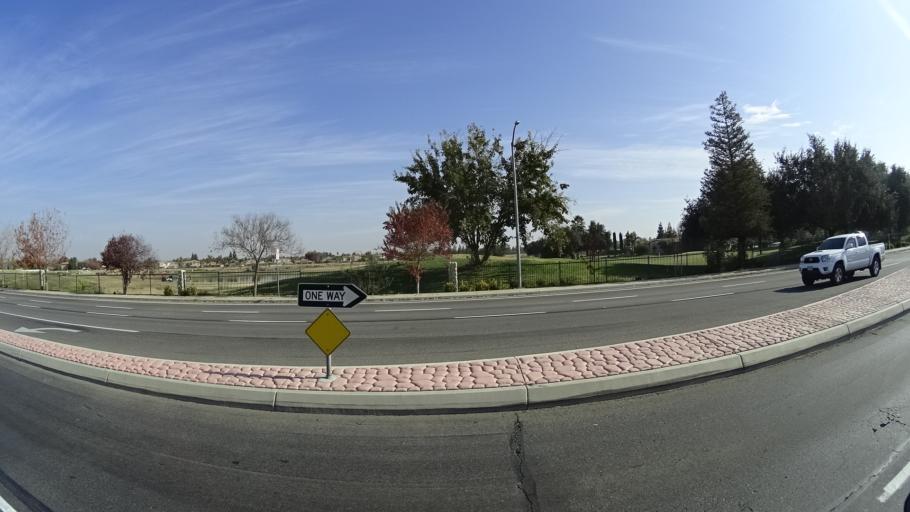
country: US
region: California
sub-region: Kern County
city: Greenacres
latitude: 35.4101
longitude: -119.1101
